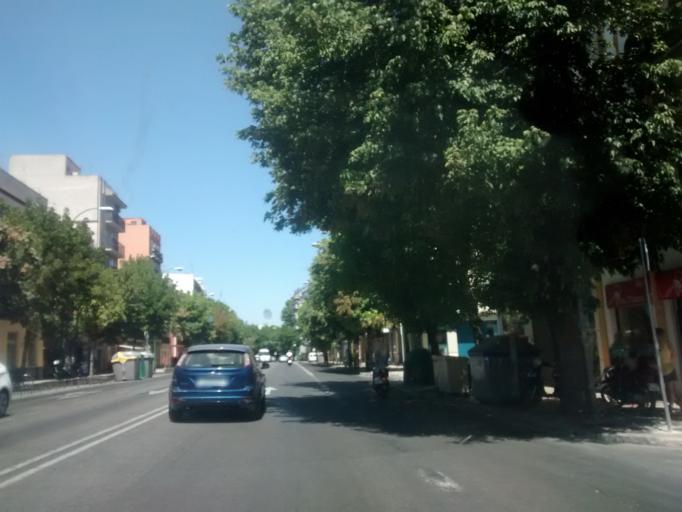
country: ES
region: Andalusia
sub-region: Provincia de Sevilla
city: Sevilla
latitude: 37.3860
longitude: -5.9859
